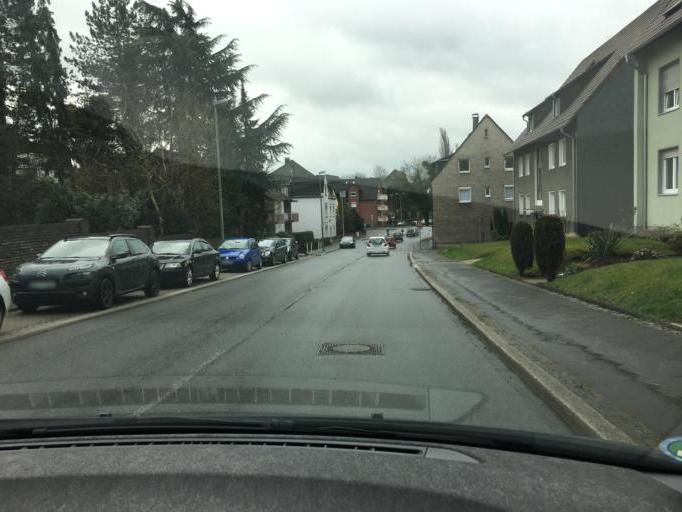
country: DE
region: North Rhine-Westphalia
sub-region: Regierungsbezirk Arnsberg
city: Bochum
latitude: 51.4942
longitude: 7.2698
